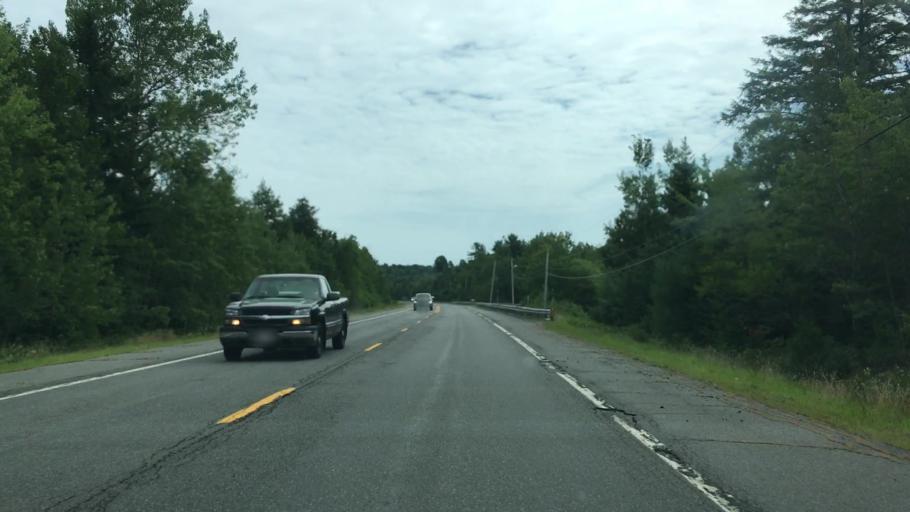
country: US
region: Maine
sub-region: Washington County
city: Calais
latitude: 45.1134
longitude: -67.4134
